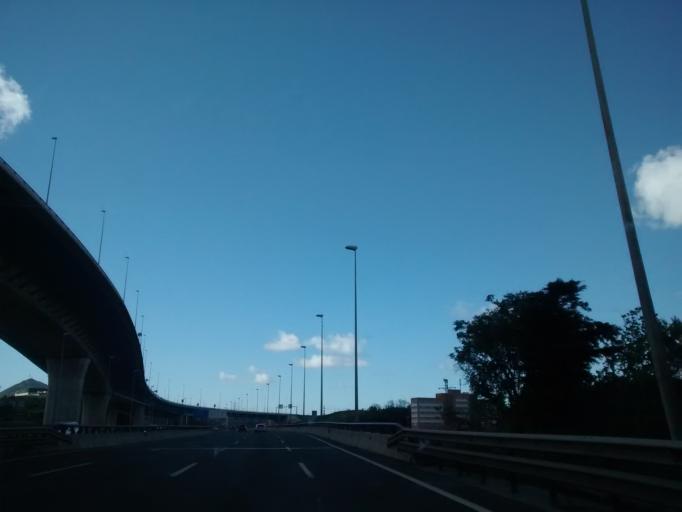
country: ES
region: Basque Country
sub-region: Bizkaia
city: Sestao
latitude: 43.2981
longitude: -3.0207
